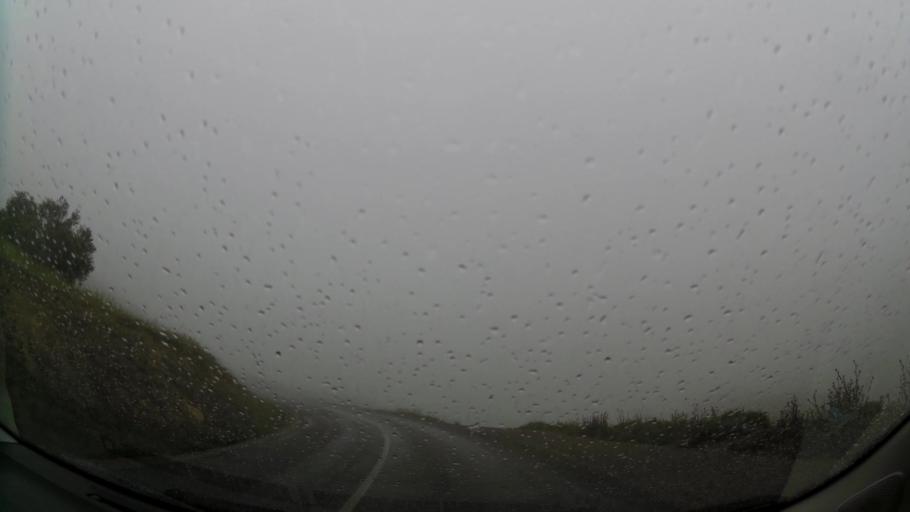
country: MA
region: Oriental
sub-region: Nador
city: Boudinar
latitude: 35.0963
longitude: -3.5326
